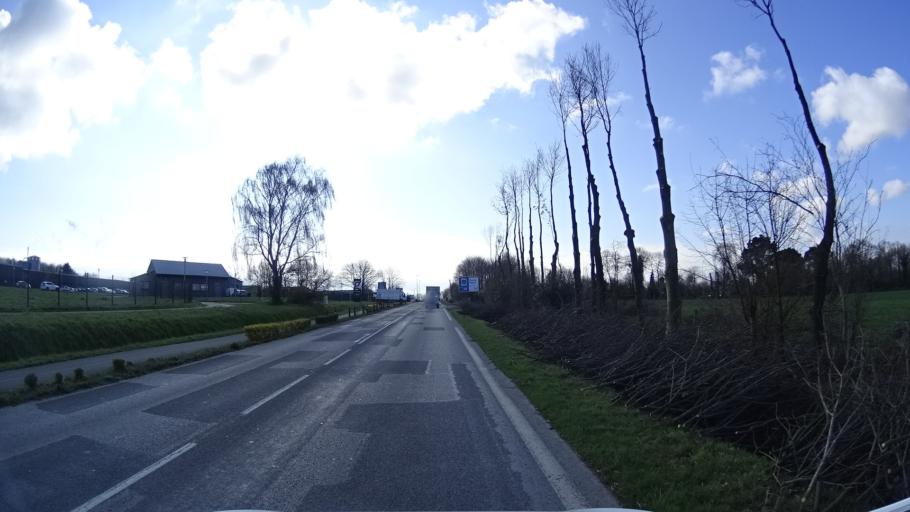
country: FR
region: Brittany
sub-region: Departement d'Ille-et-Vilaine
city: La Meziere
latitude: 48.2076
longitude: -1.7399
